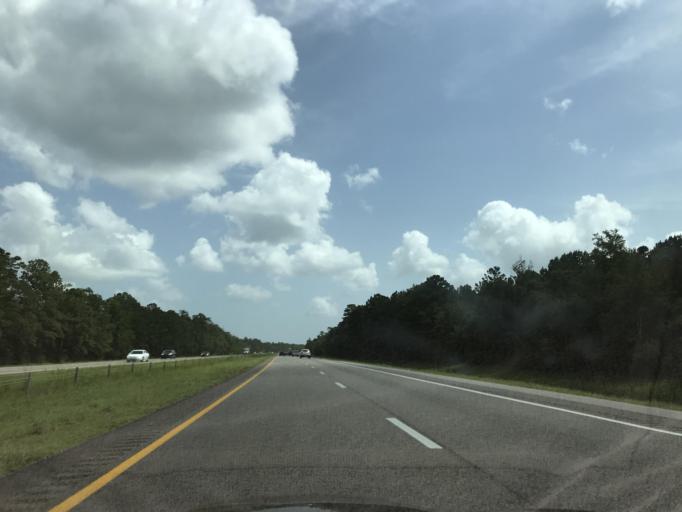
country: US
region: North Carolina
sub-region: Pender County
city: Burgaw
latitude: 34.5194
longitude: -77.8863
